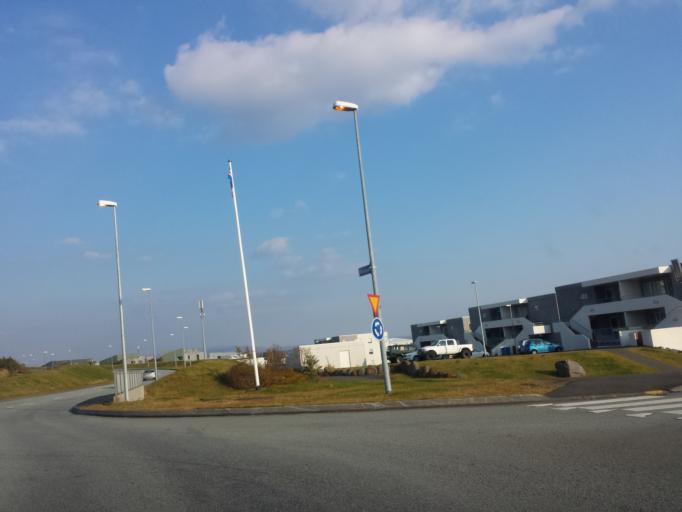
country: IS
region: Capital Region
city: Reykjavik
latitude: 64.0873
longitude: -21.8117
